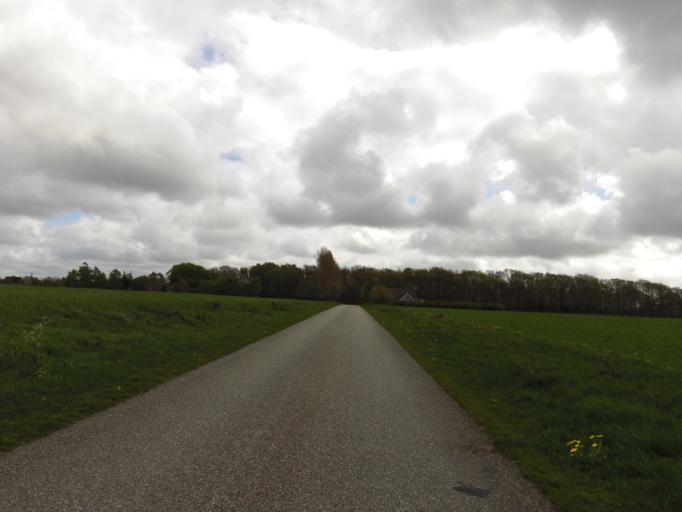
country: DK
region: South Denmark
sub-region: Tonder Kommune
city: Sherrebek
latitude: 55.2045
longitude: 8.8867
